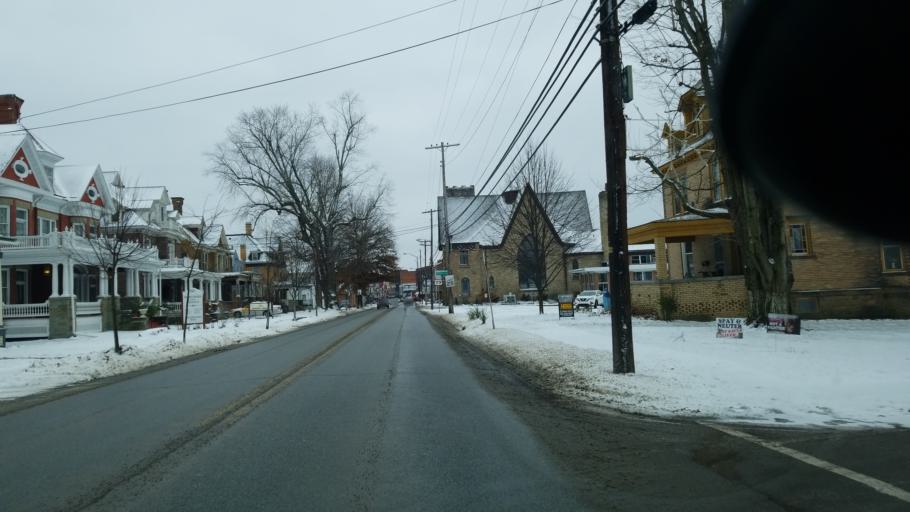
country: US
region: Pennsylvania
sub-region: Jefferson County
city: Punxsutawney
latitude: 40.9429
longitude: -78.9756
